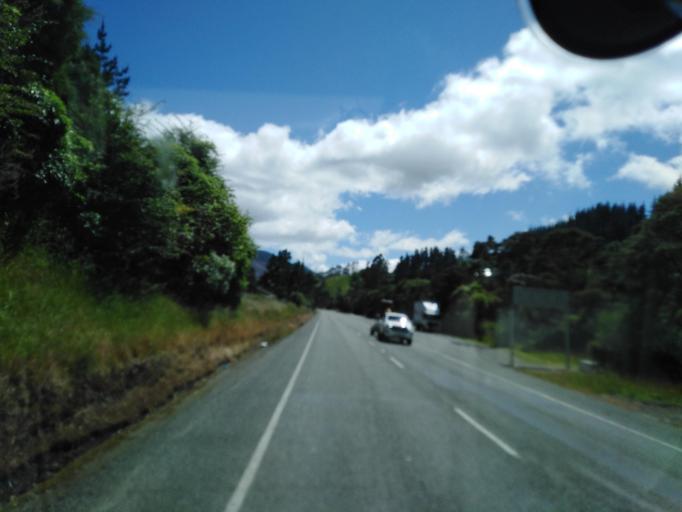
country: NZ
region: Nelson
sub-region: Nelson City
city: Nelson
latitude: -41.2235
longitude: 173.3967
